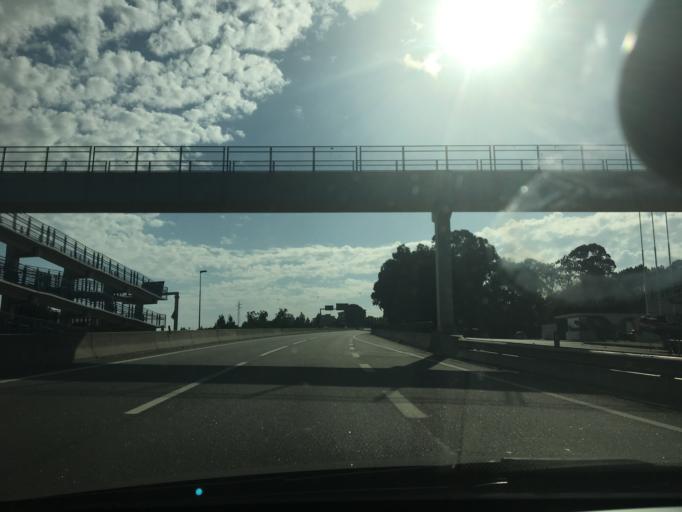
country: PT
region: Porto
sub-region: Maia
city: Leca do Bailio
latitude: 41.1982
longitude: -8.6276
